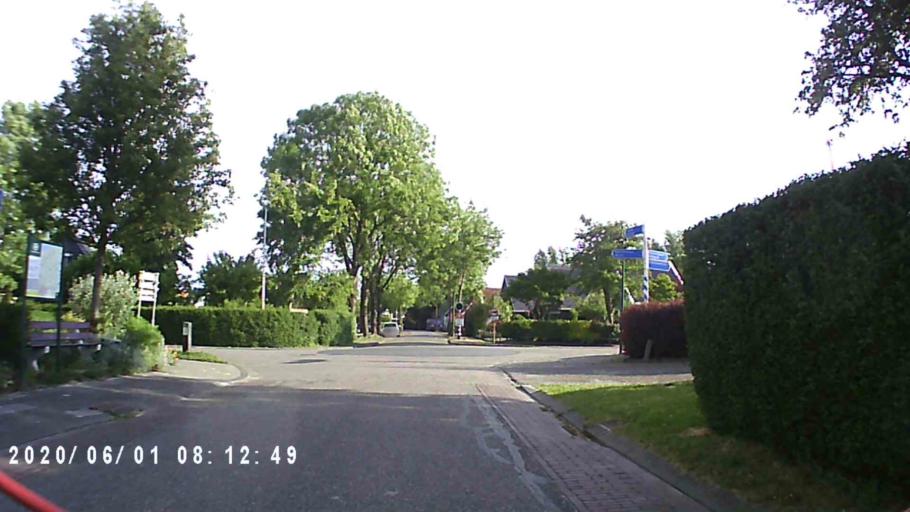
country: NL
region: Friesland
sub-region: Gemeente Ferwerderadiel
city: Burdaard
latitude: 53.2937
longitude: 5.8802
